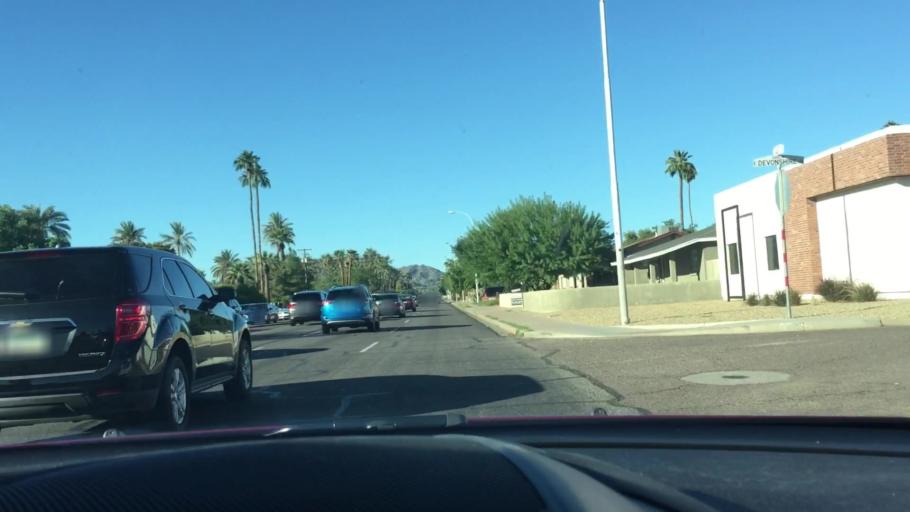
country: US
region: Arizona
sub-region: Maricopa County
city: Paradise Valley
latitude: 33.4971
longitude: -111.9868
